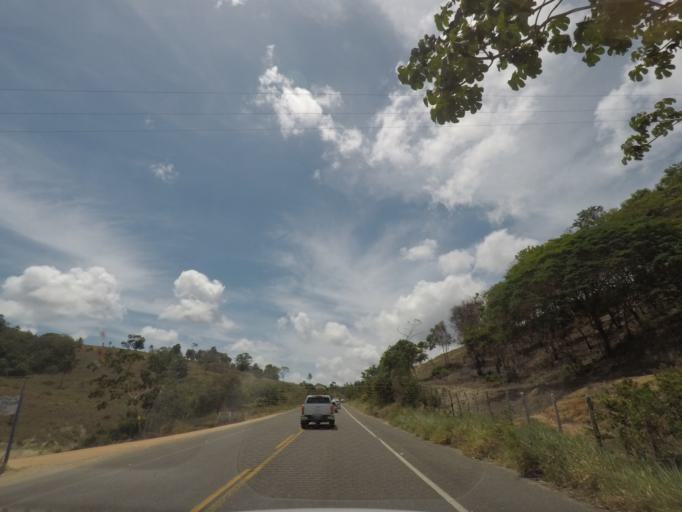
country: BR
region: Sergipe
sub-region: Indiaroba
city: Indiaroba
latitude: -11.4965
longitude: -37.4914
